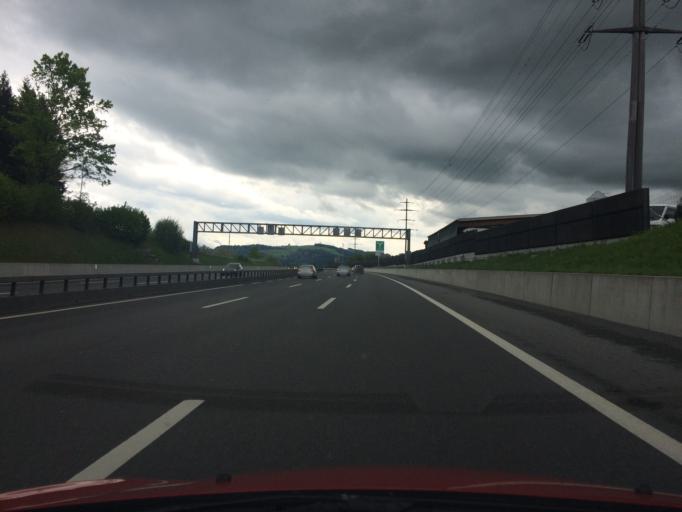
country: CH
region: Zug
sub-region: Zug
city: Hunenberg
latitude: 47.1782
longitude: 8.4334
